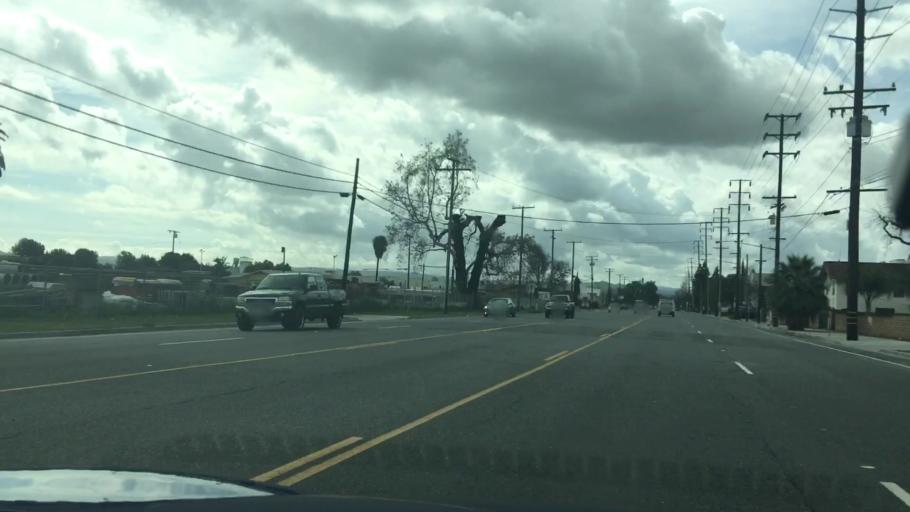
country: US
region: California
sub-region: Riverside County
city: Highgrove
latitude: 34.0183
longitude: -117.3627
